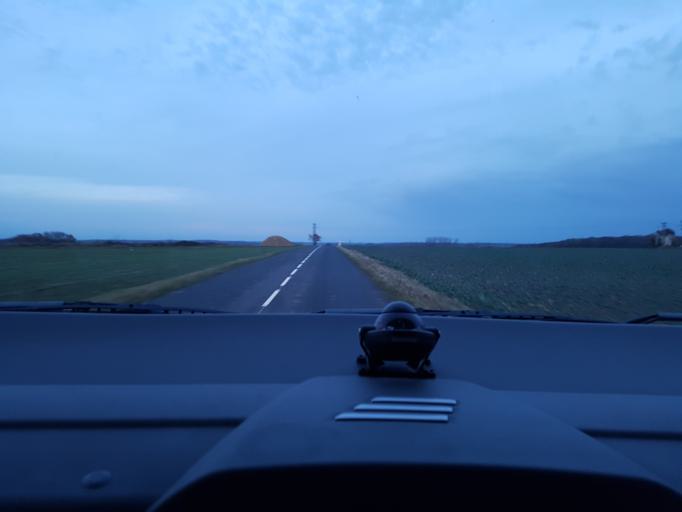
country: FR
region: Picardie
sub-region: Departement de la Somme
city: Beauquesne
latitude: 50.0717
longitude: 2.4205
